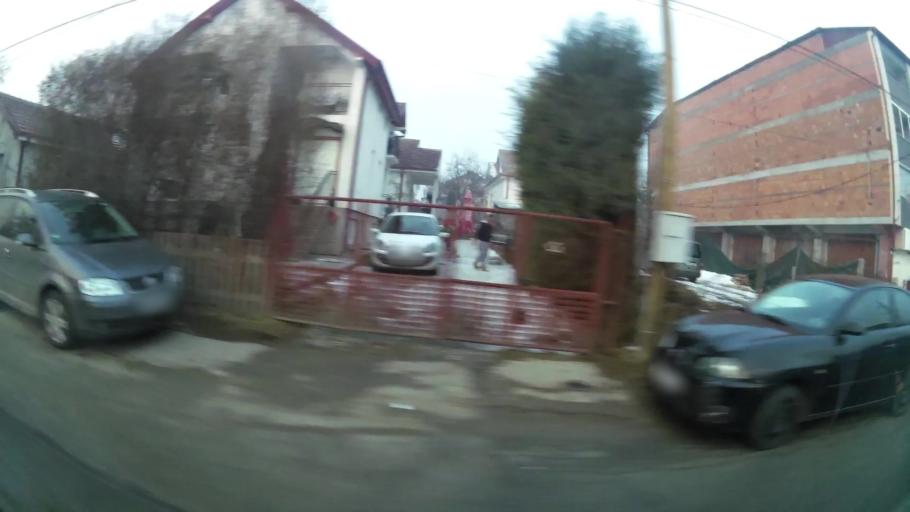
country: MK
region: Suto Orizari
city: Suto Orizare
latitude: 42.0259
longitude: 21.4115
